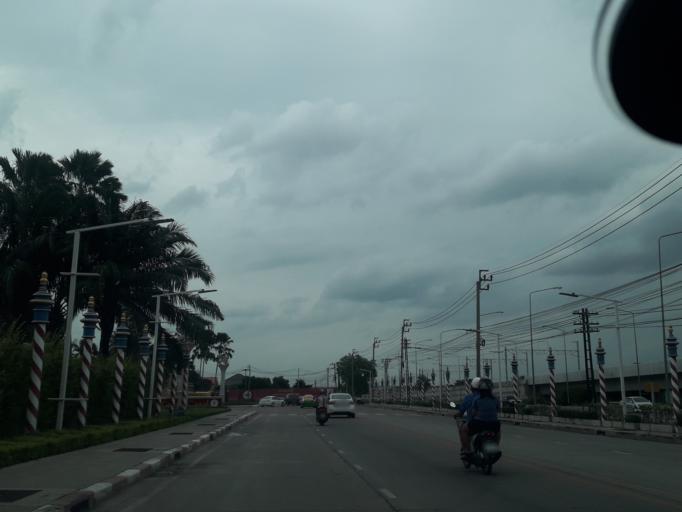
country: TH
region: Bangkok
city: Don Mueang
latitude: 13.9400
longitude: 100.6077
